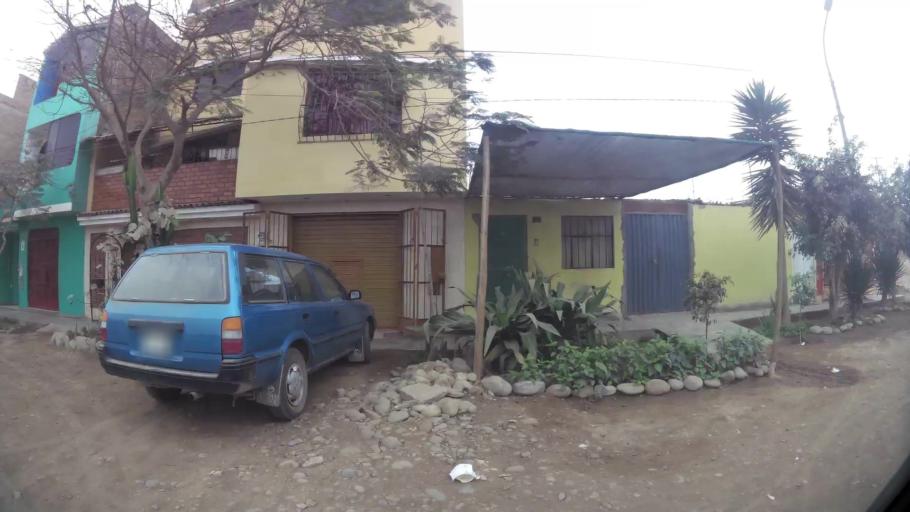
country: PE
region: Lima
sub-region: Provincia de Huaral
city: Huaral
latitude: -11.4960
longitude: -77.1984
